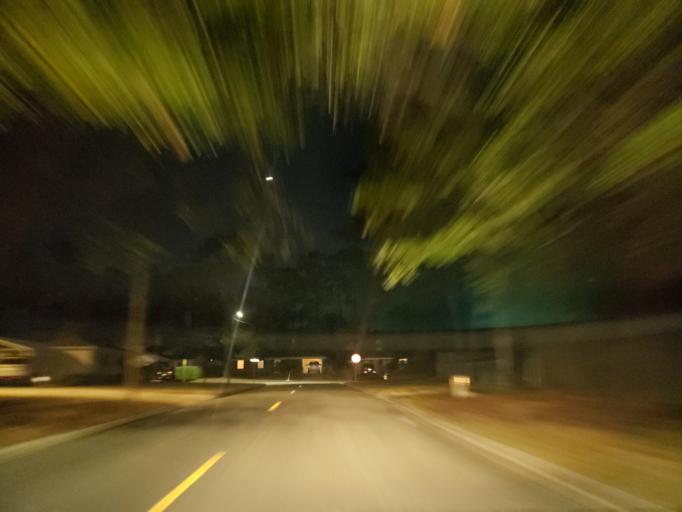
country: US
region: Georgia
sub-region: Chatham County
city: Montgomery
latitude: 31.9878
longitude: -81.1535
